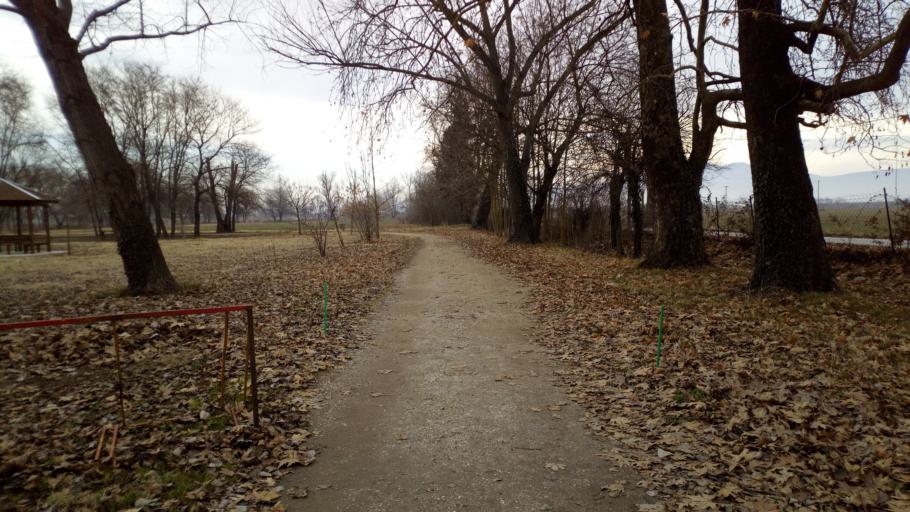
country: GR
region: Central Macedonia
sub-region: Nomos Thessalonikis
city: Lagkadas
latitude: 40.7324
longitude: 23.0845
